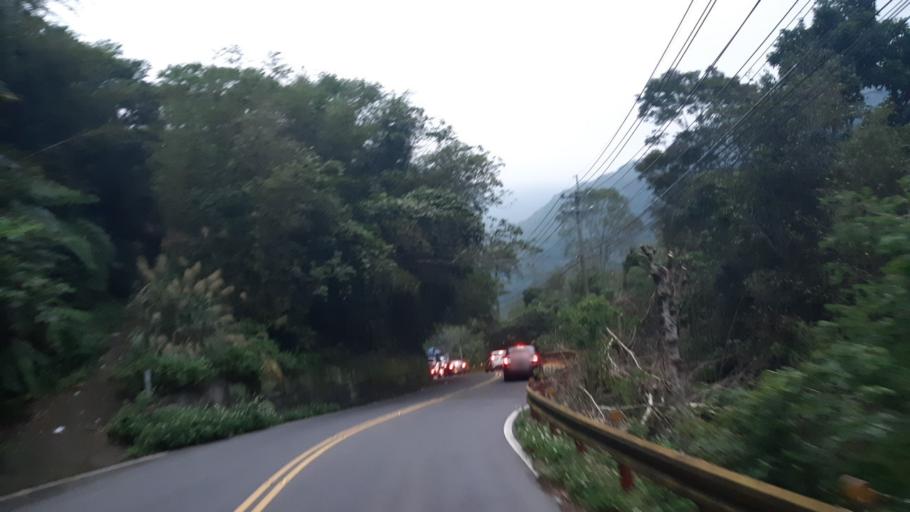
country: TW
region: Taiwan
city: Daxi
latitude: 24.7003
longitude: 121.2155
